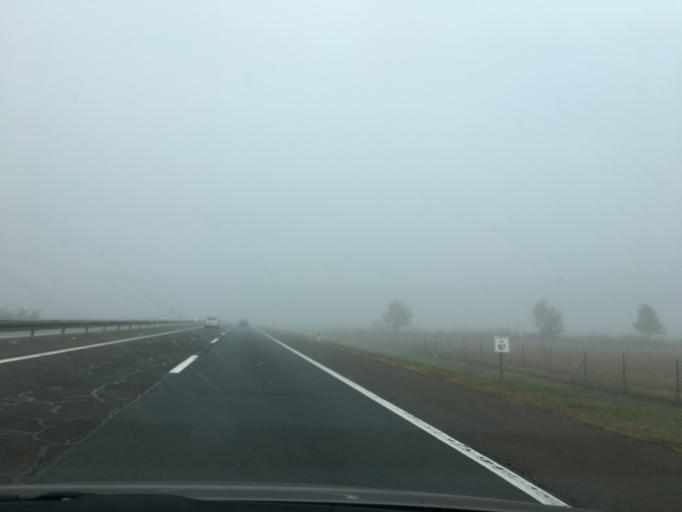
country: RS
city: Novi Banovci
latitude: 44.9566
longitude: 20.2580
